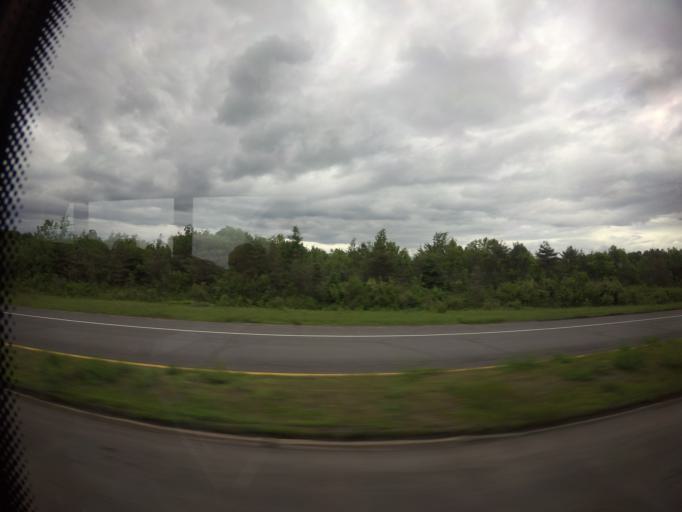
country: CA
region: Quebec
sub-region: Chaudiere-Appalaches
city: Saint-Antoine-de-Tilly
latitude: 46.5778
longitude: -71.5646
